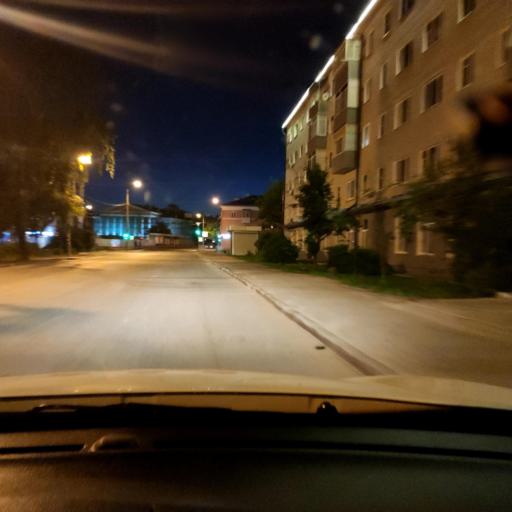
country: RU
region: Tatarstan
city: Osinovo
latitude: 55.8196
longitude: 48.9001
